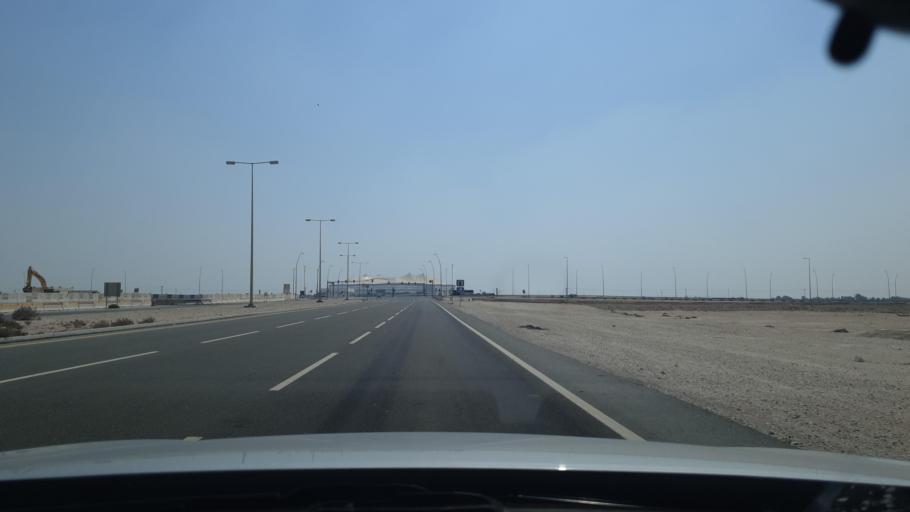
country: QA
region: Al Khawr
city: Al Khawr
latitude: 25.6676
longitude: 51.4738
